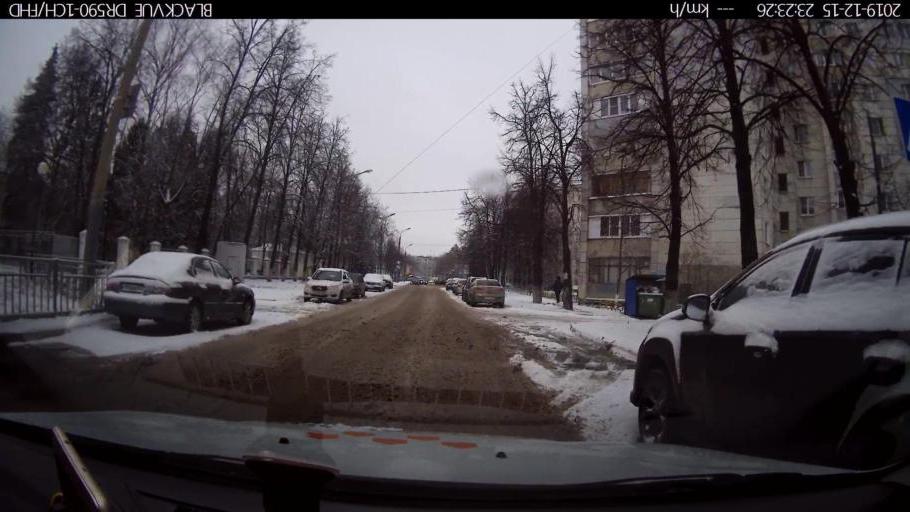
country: RU
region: Nizjnij Novgorod
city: Nizhniy Novgorod
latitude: 56.3160
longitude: 43.8719
